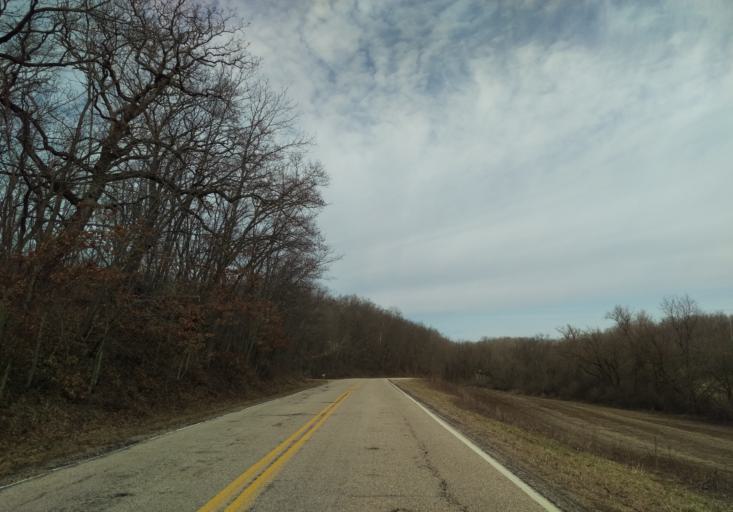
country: US
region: Wisconsin
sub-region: Dane County
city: Mount Horeb
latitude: 43.0503
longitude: -89.7549
